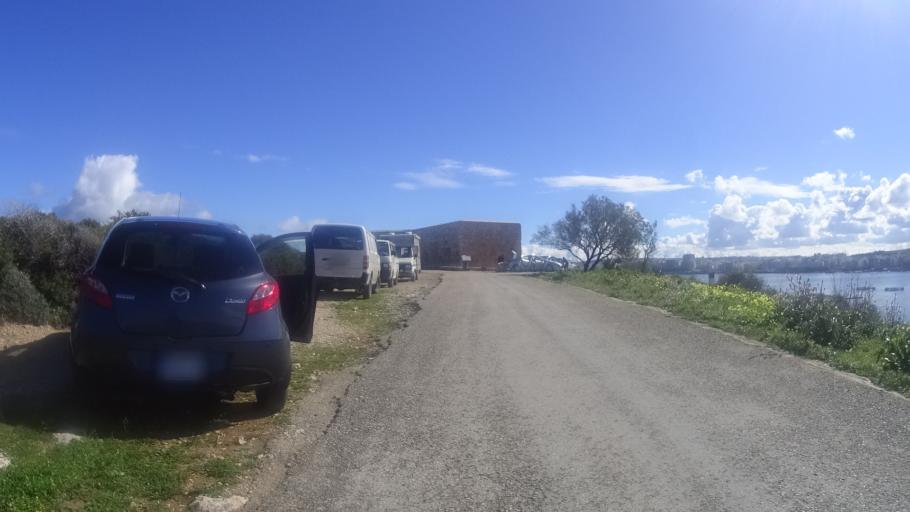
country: MT
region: Saint Paul's Bay
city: San Pawl il-Bahar
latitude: 35.9586
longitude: 14.3941
